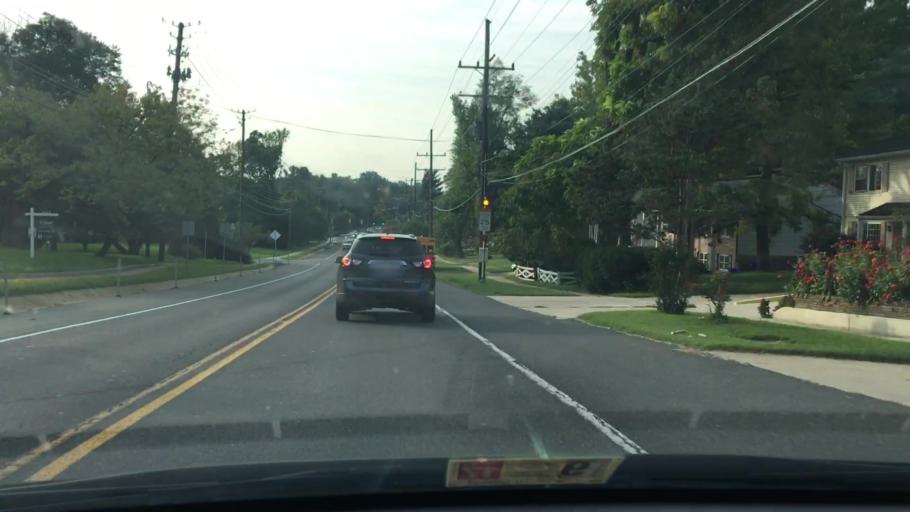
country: US
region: Maryland
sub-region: Montgomery County
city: Rockville
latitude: 39.0496
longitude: -77.1635
